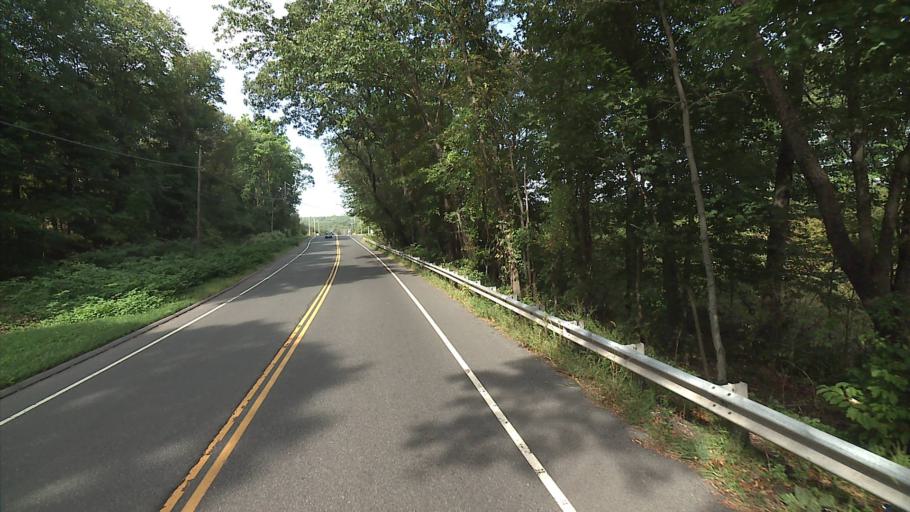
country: US
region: Connecticut
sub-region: New Haven County
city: Oxford
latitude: 41.3865
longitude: -73.1825
